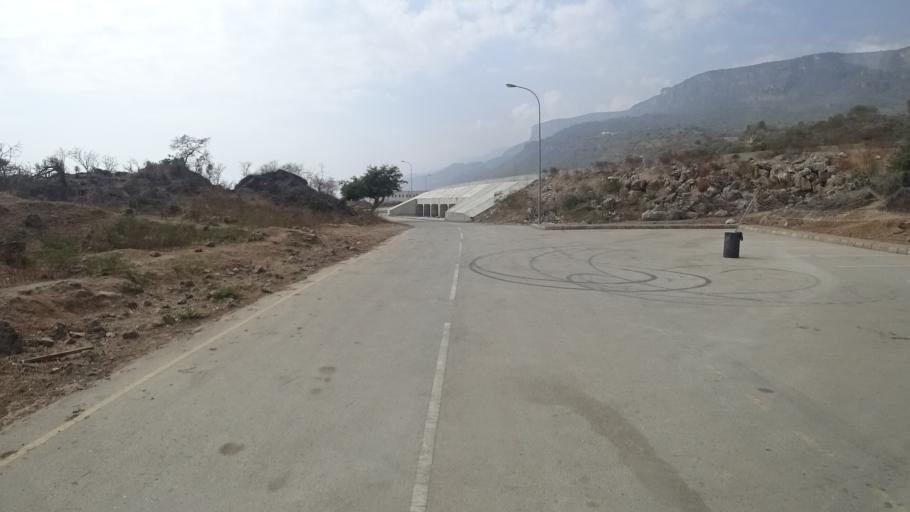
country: YE
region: Al Mahrah
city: Hawf
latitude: 16.7079
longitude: 53.2595
